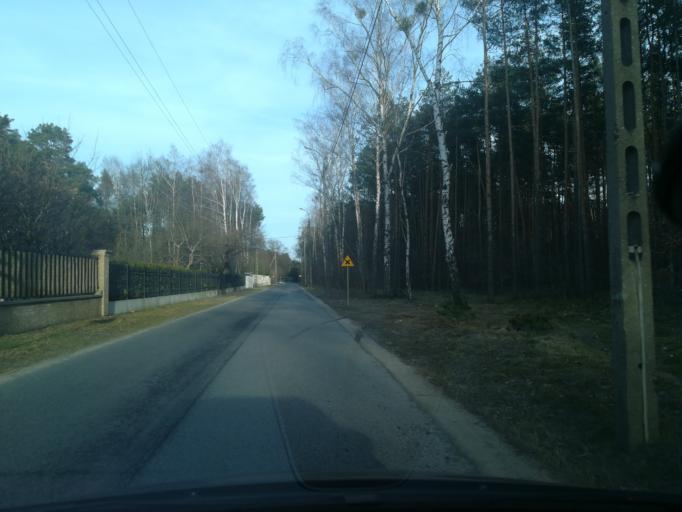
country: PL
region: Masovian Voivodeship
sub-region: Powiat piaseczynski
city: Konstancin-Jeziorna
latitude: 52.0706
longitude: 21.0955
